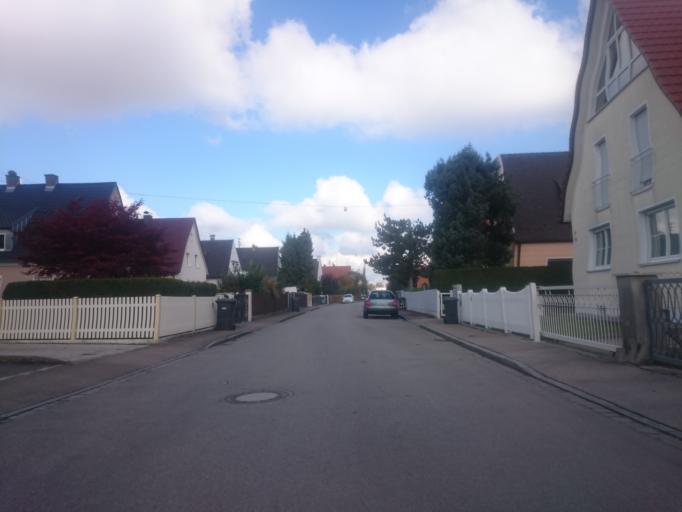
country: DE
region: Bavaria
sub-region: Swabia
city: Augsburg
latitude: 48.3770
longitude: 10.9412
